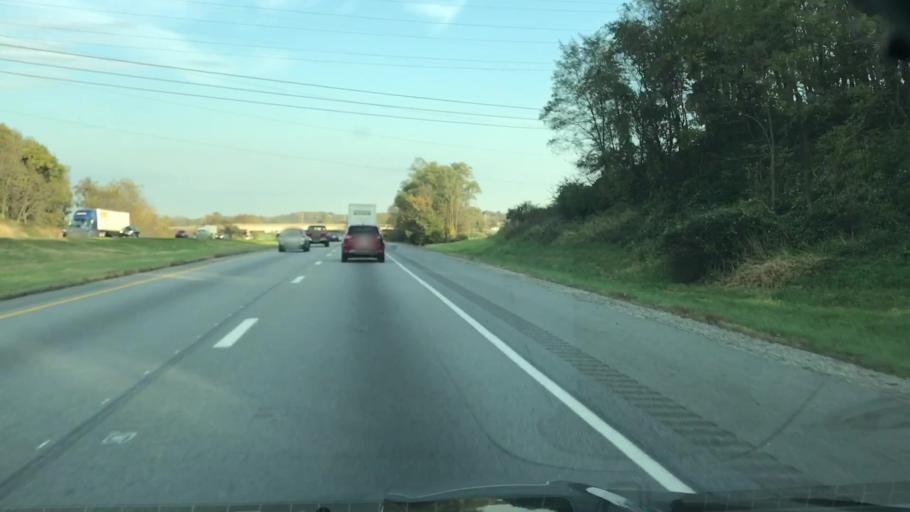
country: US
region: Pennsylvania
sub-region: Cumberland County
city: Schlusser
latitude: 40.2426
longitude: -77.1056
